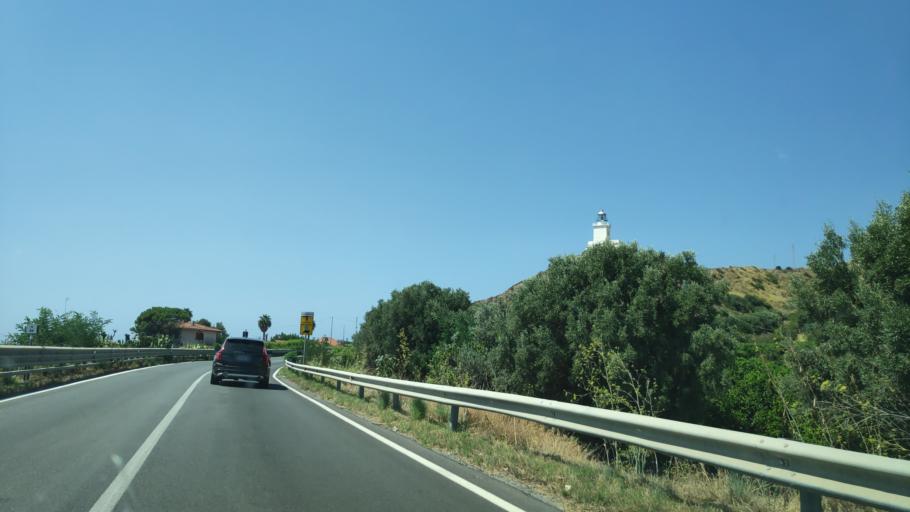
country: IT
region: Calabria
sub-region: Provincia di Reggio Calabria
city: Weather Station
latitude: 37.9264
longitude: 16.0637
